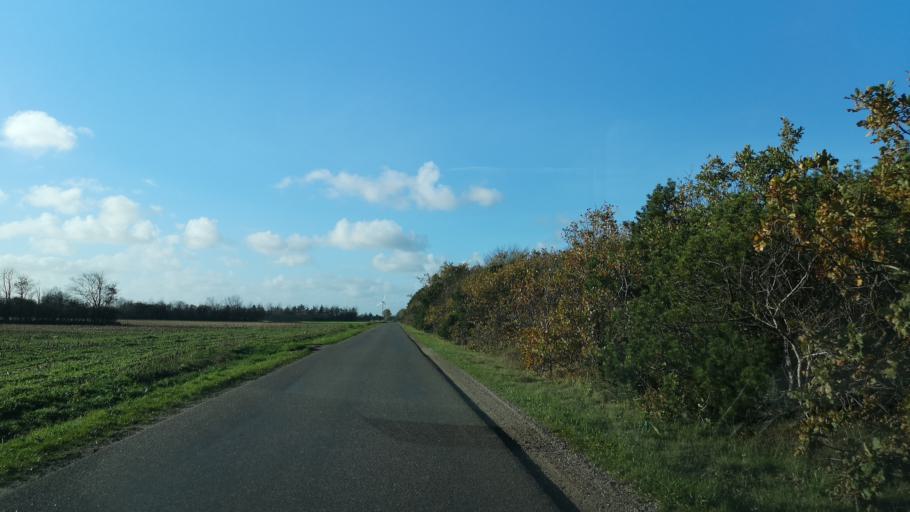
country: DK
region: Central Jutland
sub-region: Ringkobing-Skjern Kommune
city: Skjern
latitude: 55.8322
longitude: 8.3767
